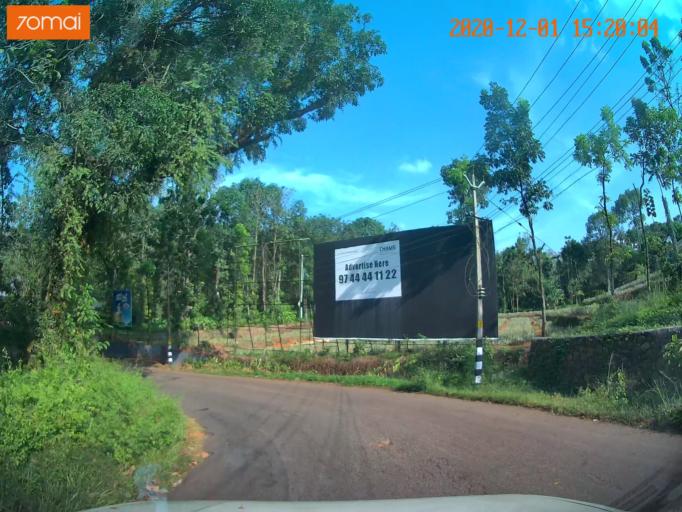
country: IN
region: Kerala
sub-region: Ernakulam
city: Ramamangalam
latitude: 9.9409
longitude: 76.5380
